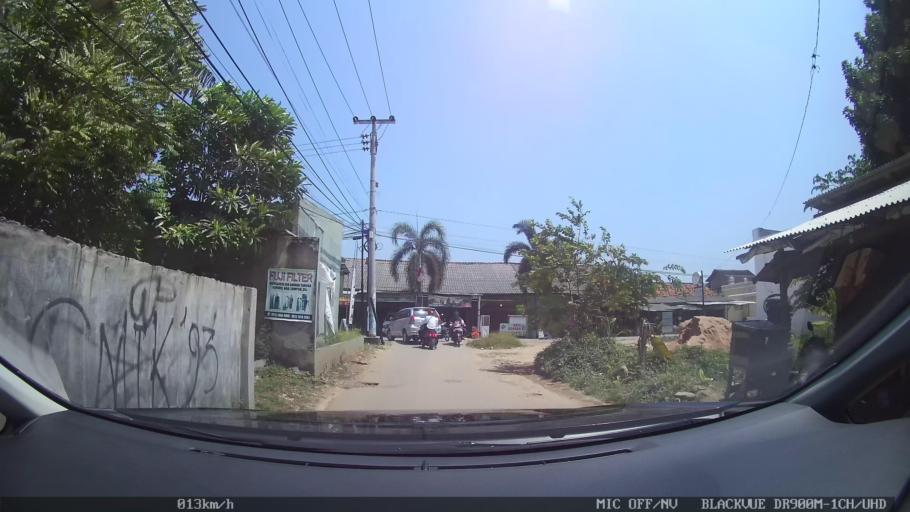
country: ID
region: Lampung
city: Kedaton
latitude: -5.3601
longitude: 105.2741
